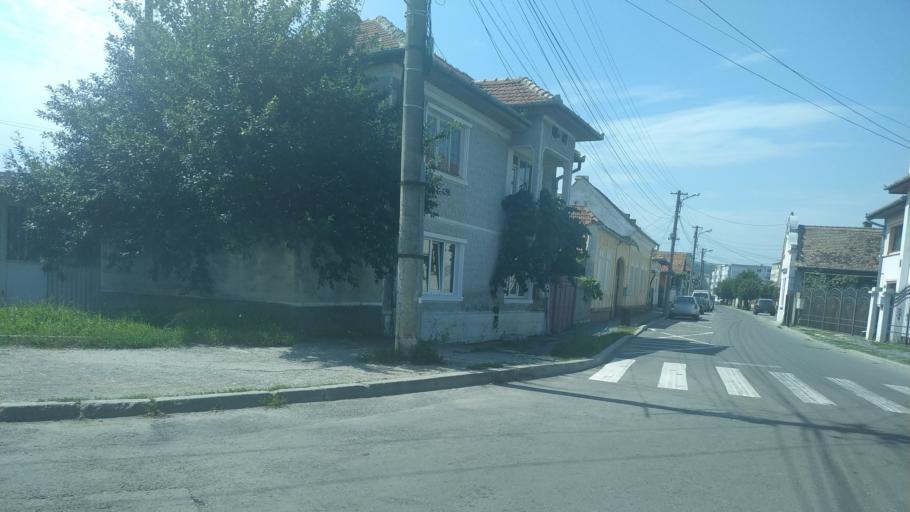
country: RO
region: Brasov
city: Fogarasch
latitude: 45.8389
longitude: 24.9704
